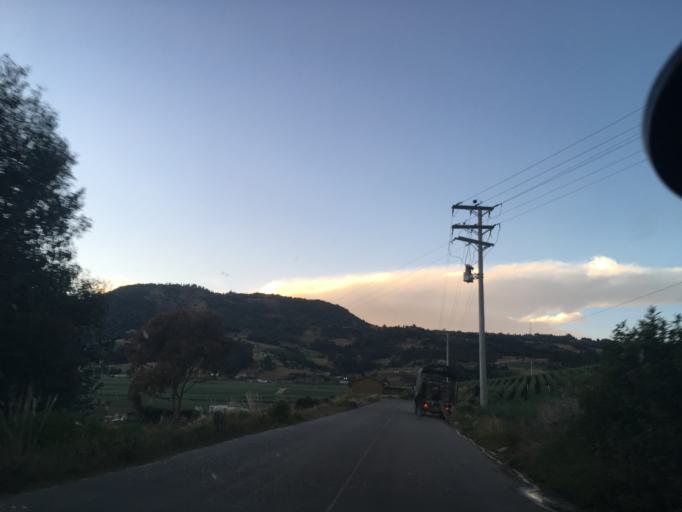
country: CO
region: Boyaca
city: Aquitania
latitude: 5.5949
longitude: -72.9078
